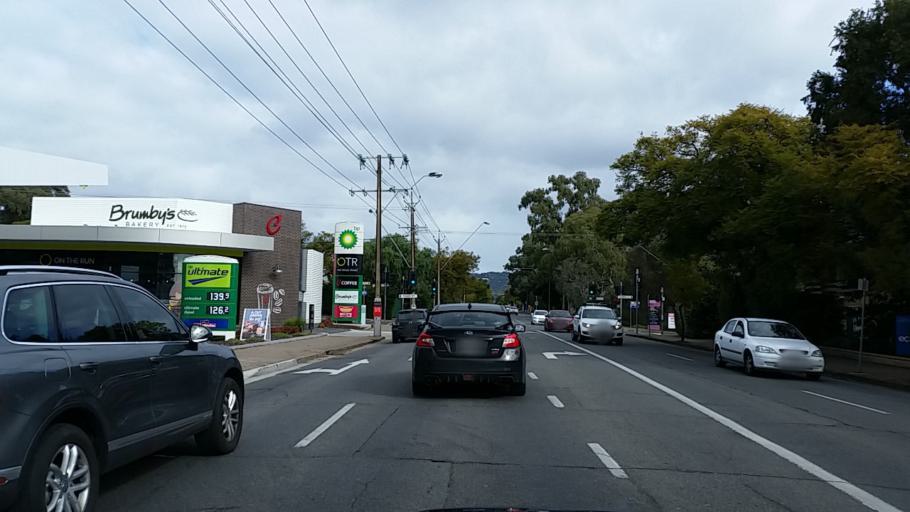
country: AU
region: South Australia
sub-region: Unley
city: Fullarton
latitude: -34.9563
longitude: 138.6258
